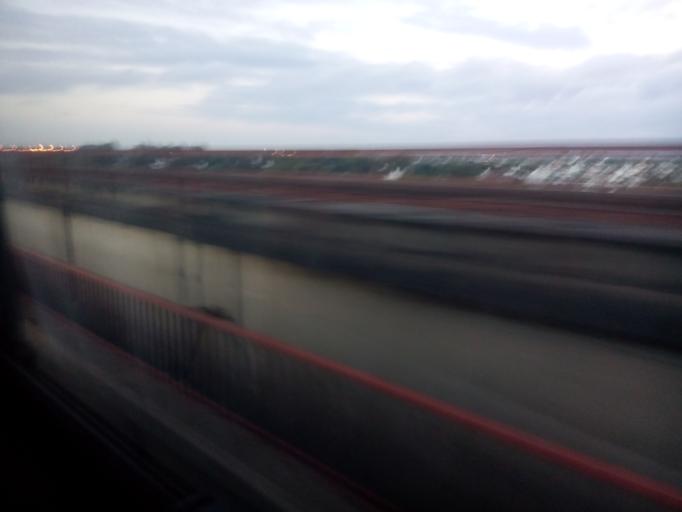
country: AR
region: Buenos Aires
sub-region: Partido de Zarate
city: Zarate
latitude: -34.1090
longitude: -59.0041
